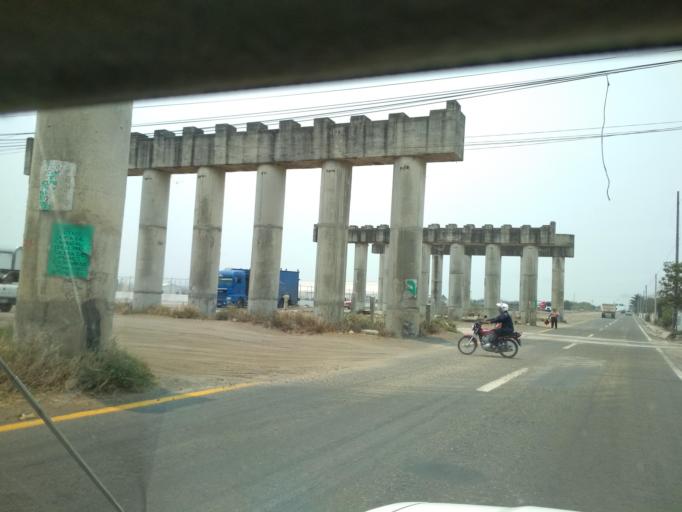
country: MX
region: Veracruz
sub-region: Veracruz
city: Delfino Victoria (Santa Fe)
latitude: 19.2032
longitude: -96.2679
